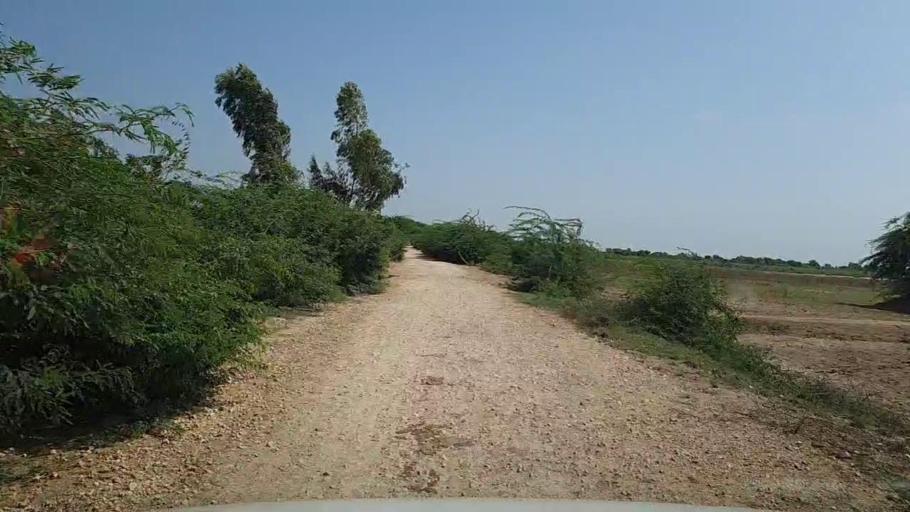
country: PK
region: Sindh
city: Kario
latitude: 24.8410
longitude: 68.7040
